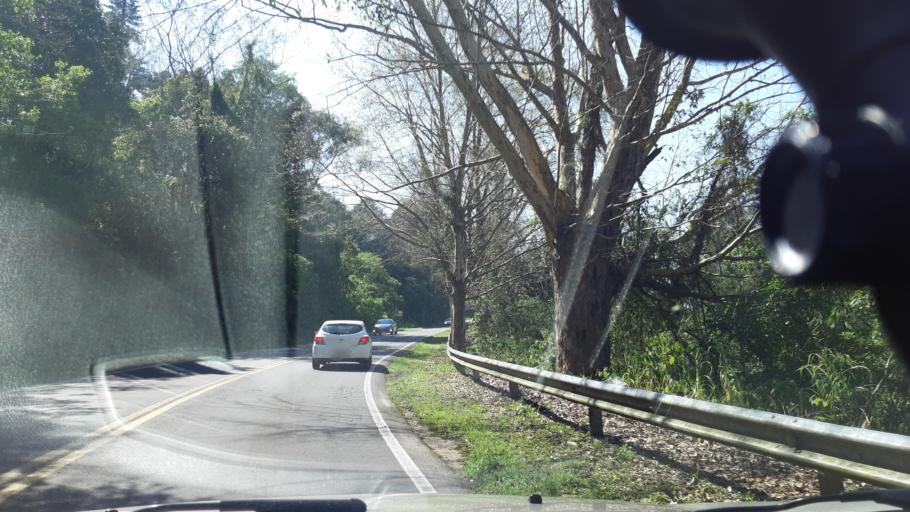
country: BR
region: Rio Grande do Sul
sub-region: Nova Petropolis
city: Nova Petropolis
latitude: -29.3965
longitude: -51.1263
